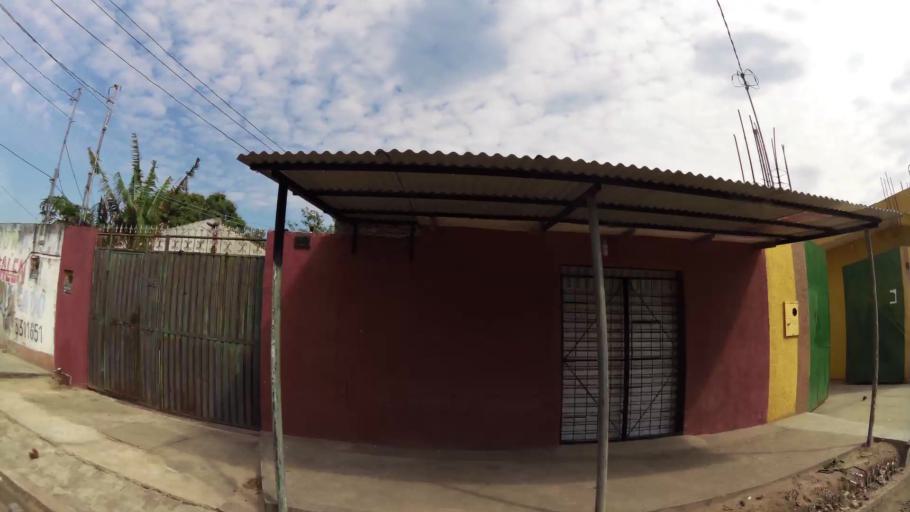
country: BO
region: Santa Cruz
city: Santa Cruz de la Sierra
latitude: -17.7300
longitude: -63.1805
